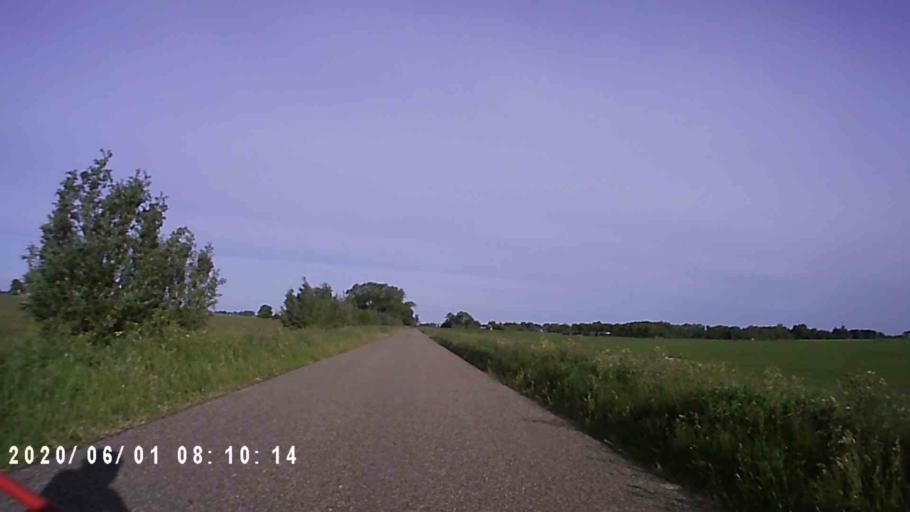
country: NL
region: Friesland
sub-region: Gemeente Ferwerderadiel
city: Burdaard
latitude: 53.2862
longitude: 5.8890
